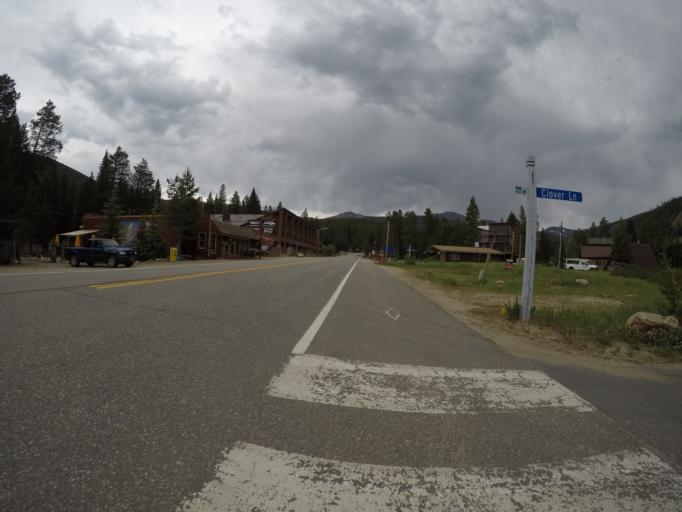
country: US
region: Colorado
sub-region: Grand County
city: Fraser
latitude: 39.8920
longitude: -105.7651
